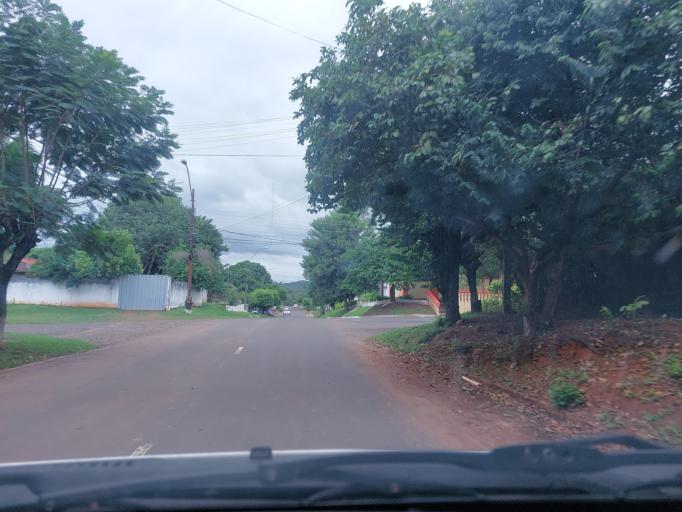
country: PY
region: San Pedro
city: Guayaybi
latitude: -24.6593
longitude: -56.4411
